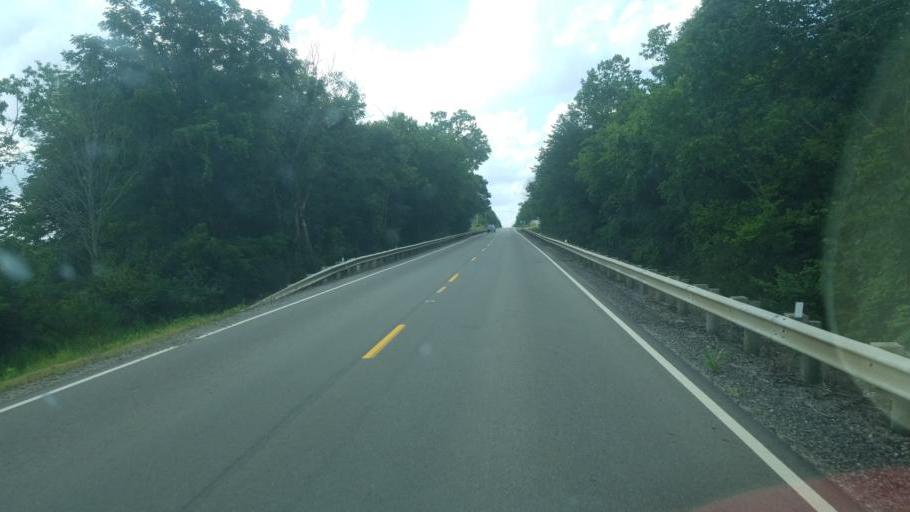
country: US
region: Ohio
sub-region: Knox County
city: Oak Hill
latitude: 40.3381
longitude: -82.1882
